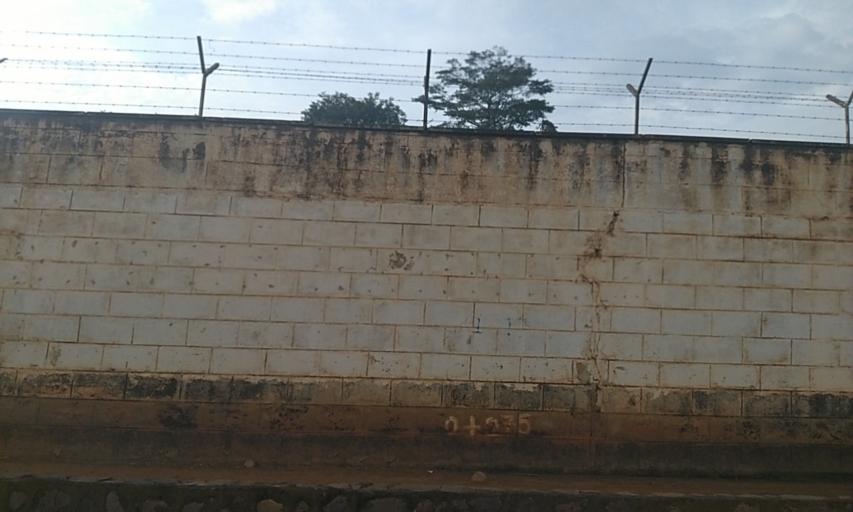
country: UG
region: Central Region
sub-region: Kampala District
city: Kampala
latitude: 0.3144
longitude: 32.5961
